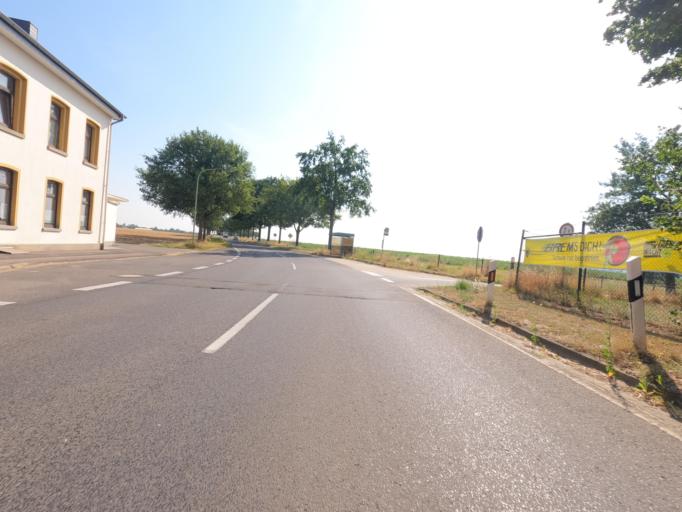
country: DE
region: North Rhine-Westphalia
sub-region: Regierungsbezirk Koln
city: Titz
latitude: 51.0037
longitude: 6.3674
